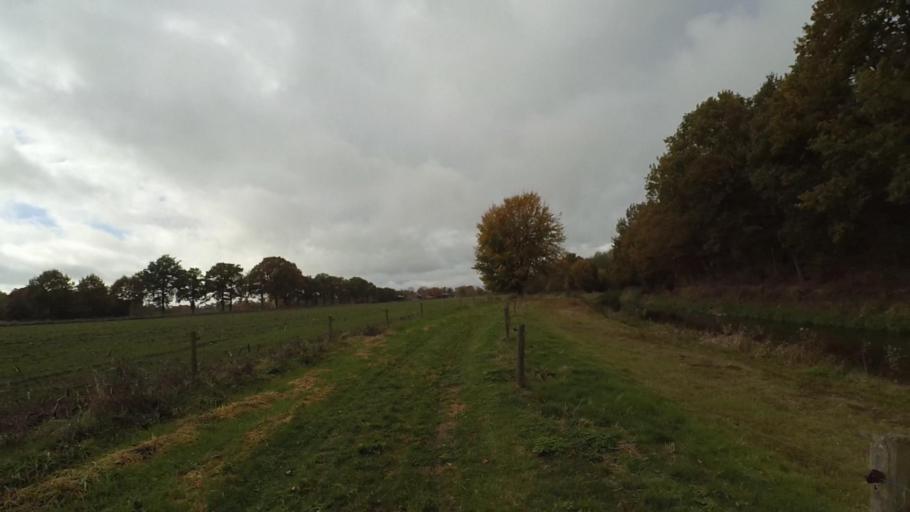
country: NL
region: Gelderland
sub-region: Gemeente Barneveld
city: Terschuur
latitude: 52.1439
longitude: 5.5238
